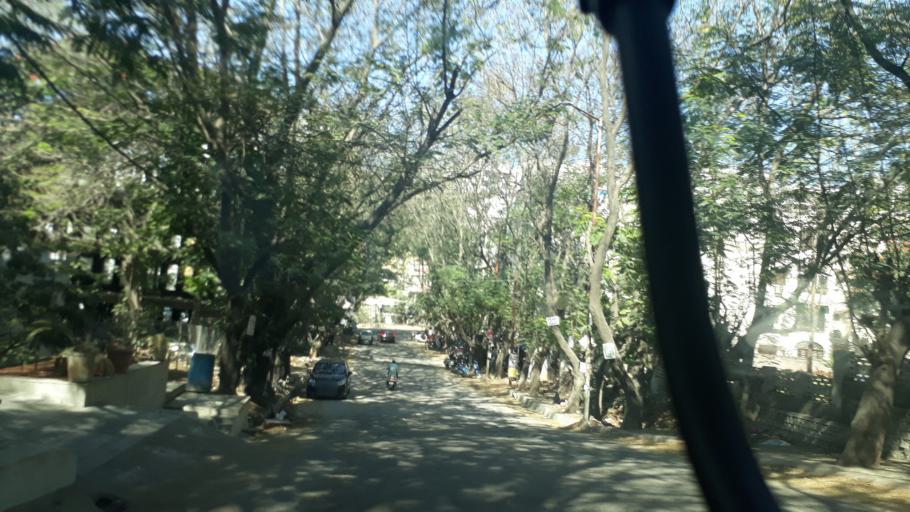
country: IN
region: Telangana
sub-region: Rangareddi
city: Kukatpalli
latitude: 17.4233
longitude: 78.4019
